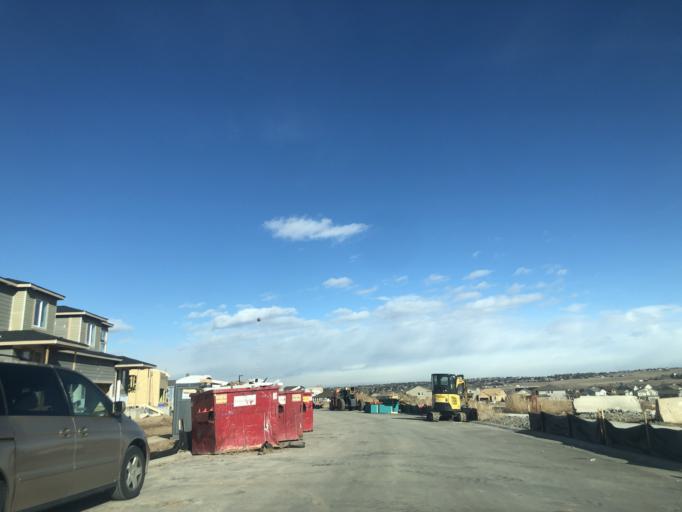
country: US
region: Colorado
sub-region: Douglas County
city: Stonegate
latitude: 39.5533
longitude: -104.8058
